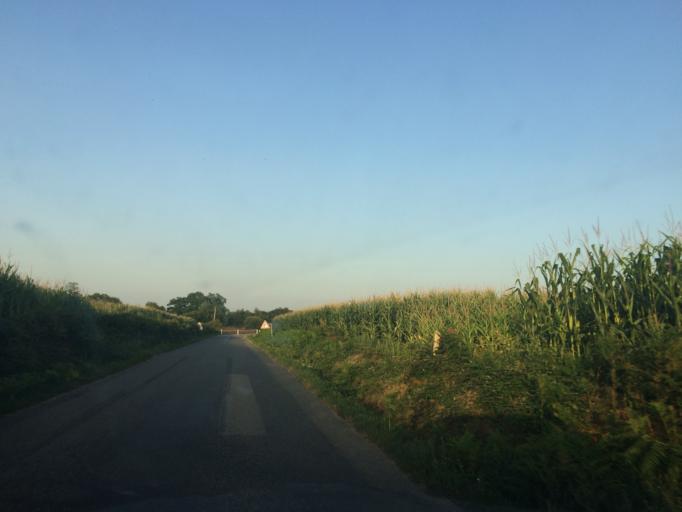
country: FR
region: Brittany
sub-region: Departement du Morbihan
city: Allaire
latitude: 47.6355
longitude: -2.1877
